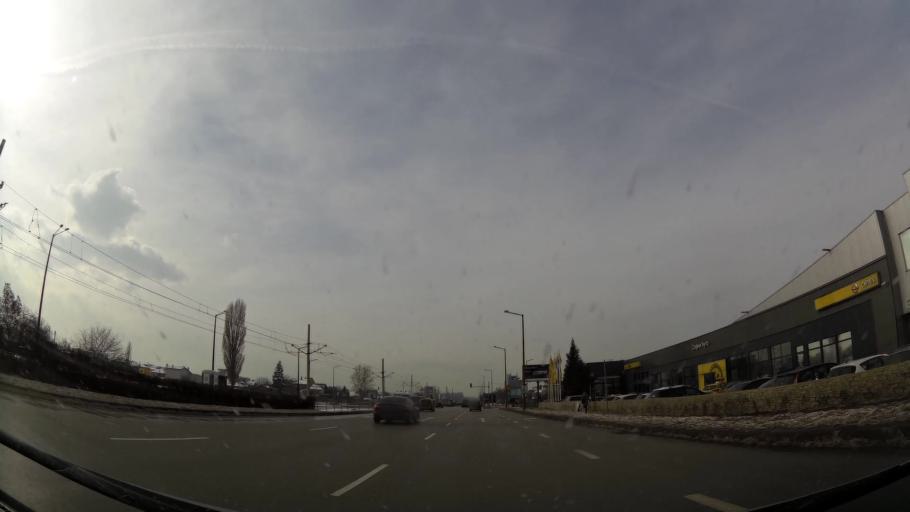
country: BG
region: Sofia-Capital
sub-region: Stolichna Obshtina
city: Sofia
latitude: 42.7035
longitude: 23.3882
